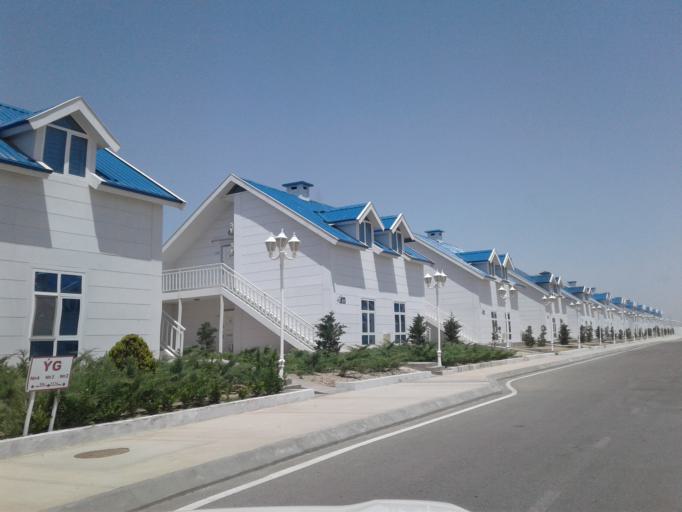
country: TM
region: Balkan
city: Turkmenbasy
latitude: 39.9867
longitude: 52.8268
